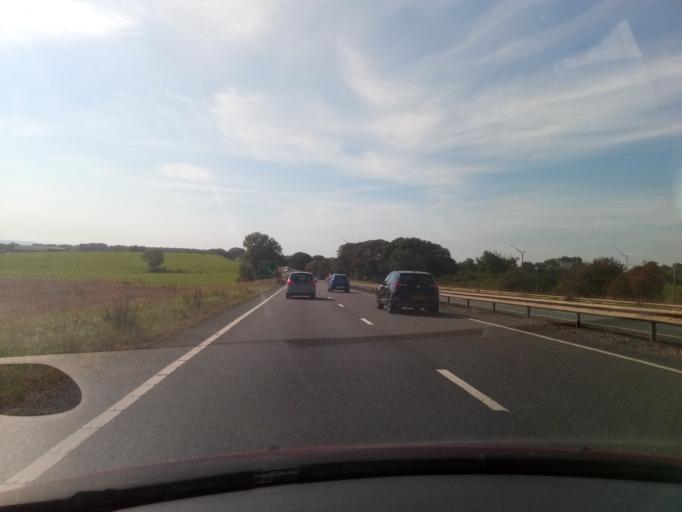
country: GB
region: England
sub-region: Hartlepool
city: Elwick
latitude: 54.6646
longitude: -1.3016
